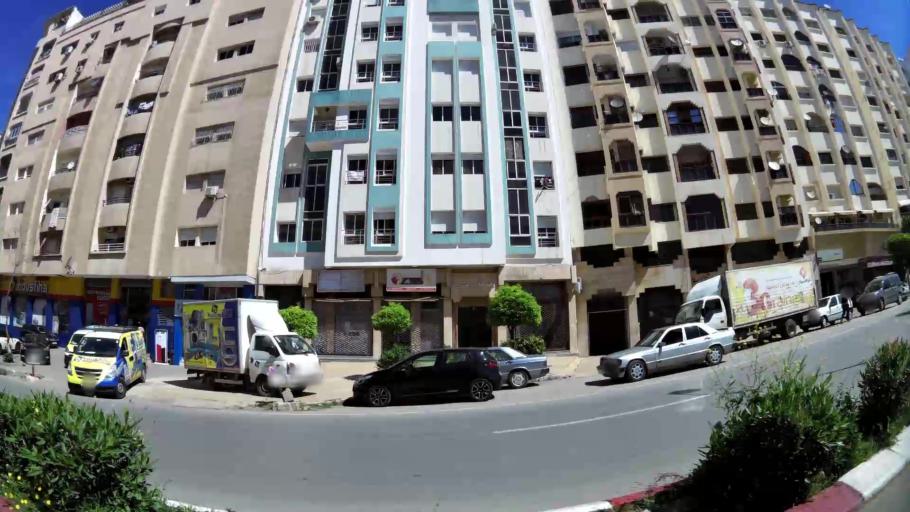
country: MA
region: Meknes-Tafilalet
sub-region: Meknes
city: Meknes
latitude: 33.8957
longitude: -5.5468
